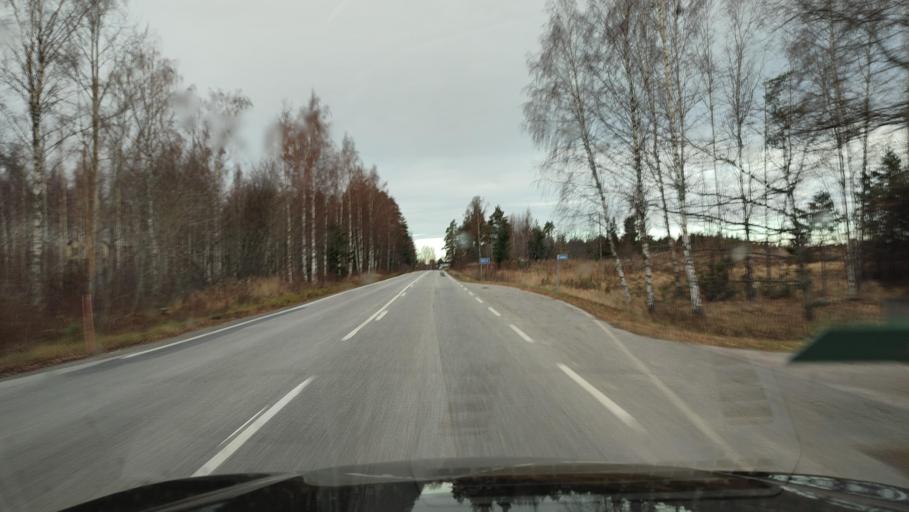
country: FI
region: Ostrobothnia
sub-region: Sydosterbotten
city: Naerpes
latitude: 62.4156
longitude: 21.3450
